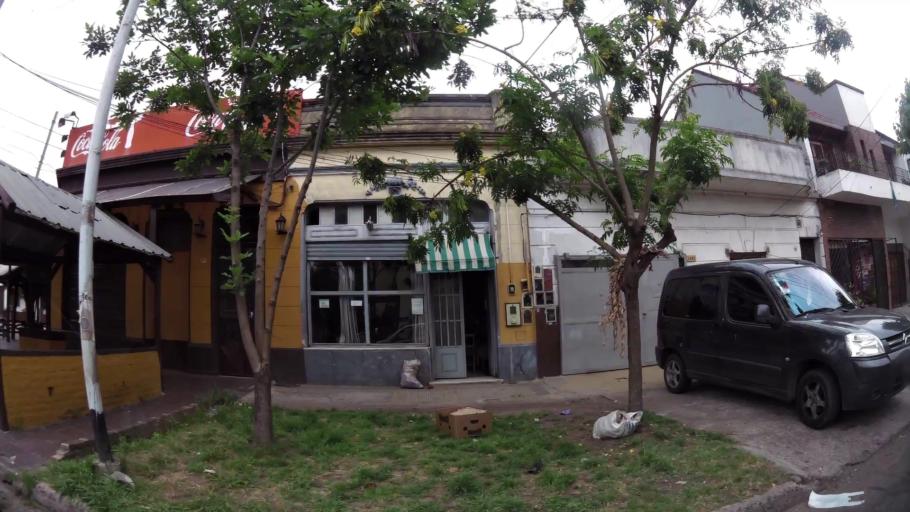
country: AR
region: Buenos Aires
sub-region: Partido de Avellaneda
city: Avellaneda
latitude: -34.6811
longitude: -58.3714
